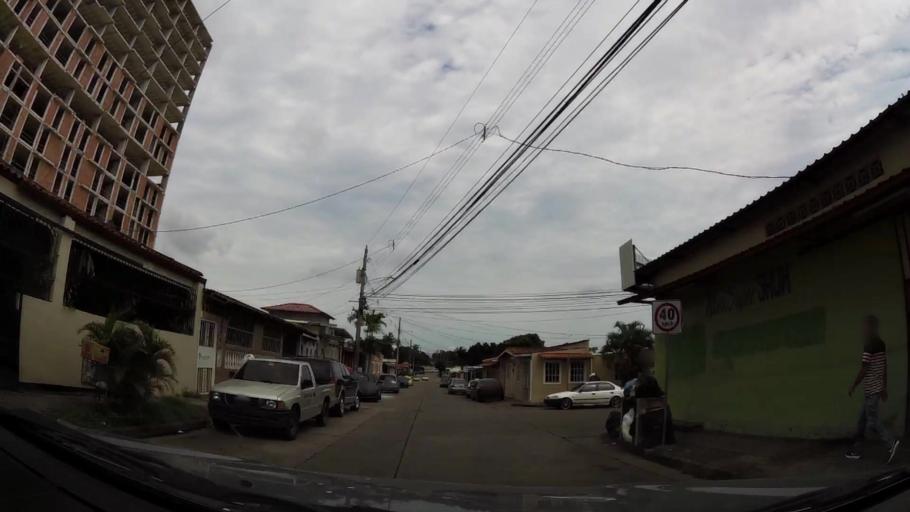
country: PA
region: Panama
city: Tocumen
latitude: 9.0582
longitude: -79.4210
